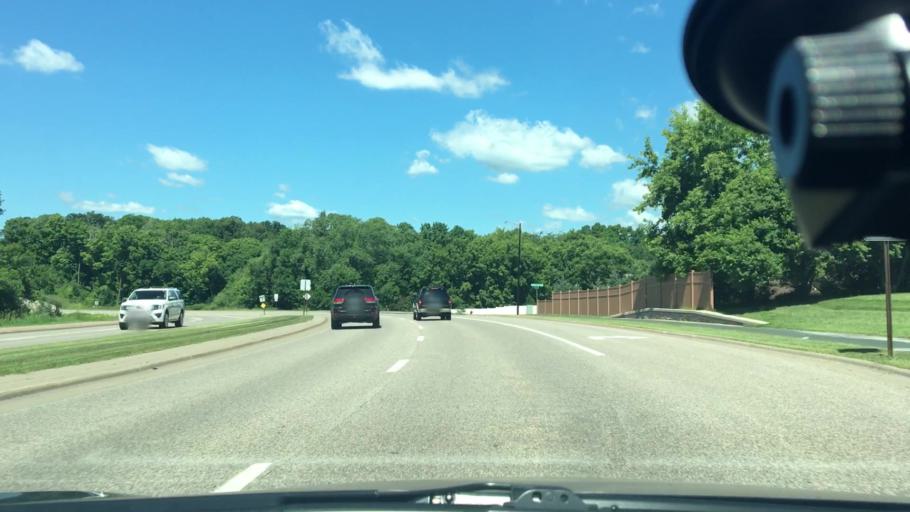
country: US
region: Minnesota
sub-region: Hennepin County
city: Maple Grove
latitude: 45.0757
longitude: -93.4624
